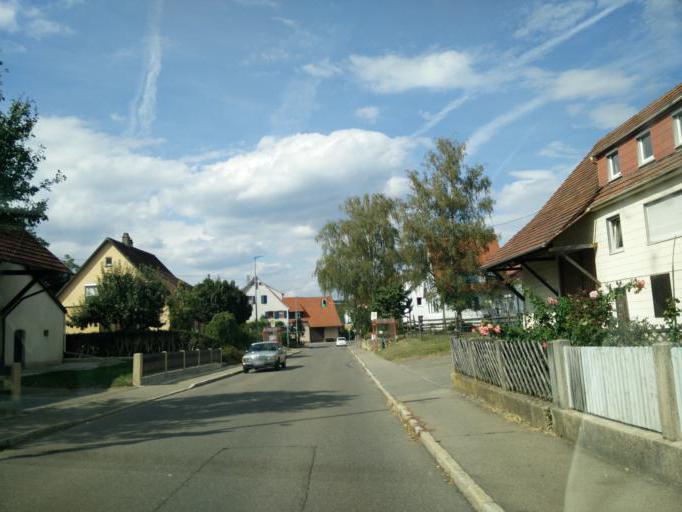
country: DE
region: Baden-Wuerttemberg
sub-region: Tuebingen Region
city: Kirchentellinsfurt
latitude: 48.5329
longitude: 9.1515
